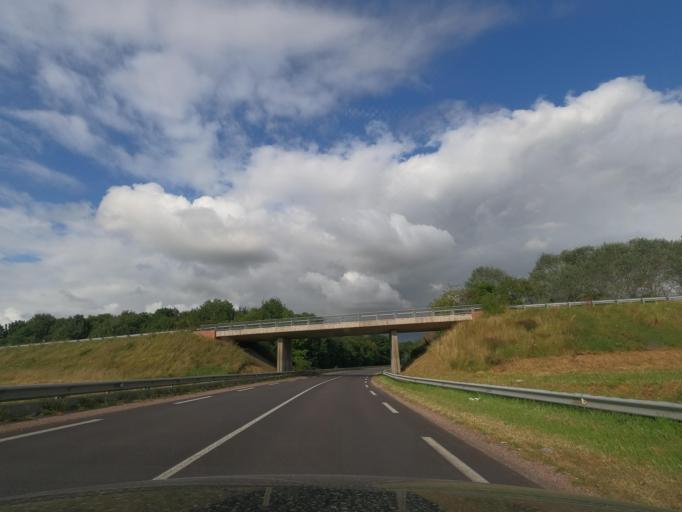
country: FR
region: Haute-Normandie
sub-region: Departement de l'Eure
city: Bernay
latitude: 49.1044
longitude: 0.5770
